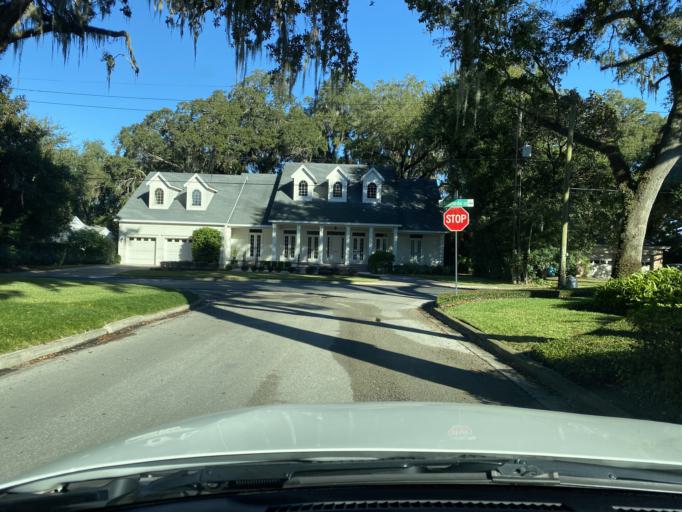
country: US
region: Florida
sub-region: Orange County
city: Orlando
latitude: 28.5568
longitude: -81.4028
